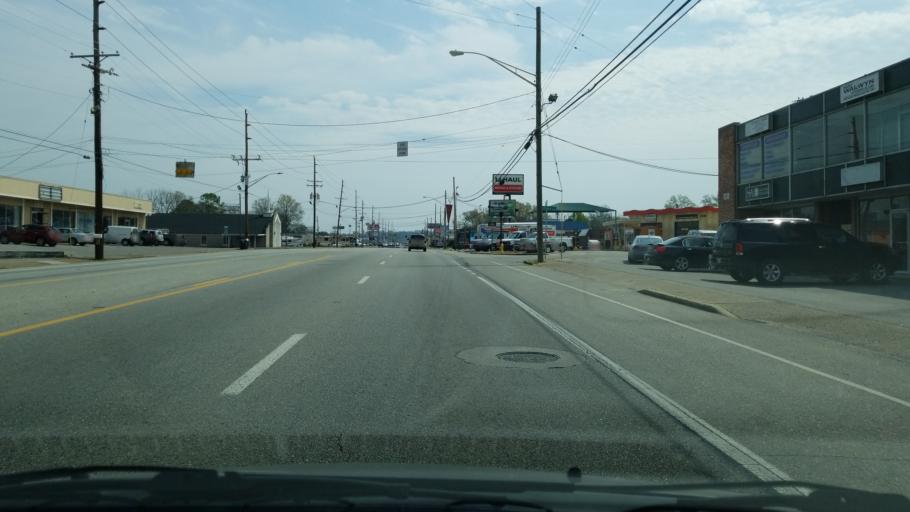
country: US
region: Tennessee
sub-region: Hamilton County
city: East Ridge
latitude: 34.9904
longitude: -85.2201
